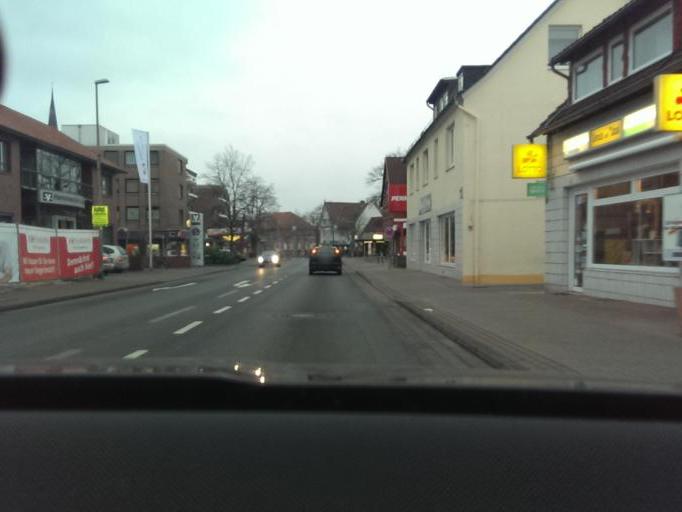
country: DE
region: Lower Saxony
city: Isernhagen Farster Bauerschaft
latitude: 52.4916
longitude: 9.8590
